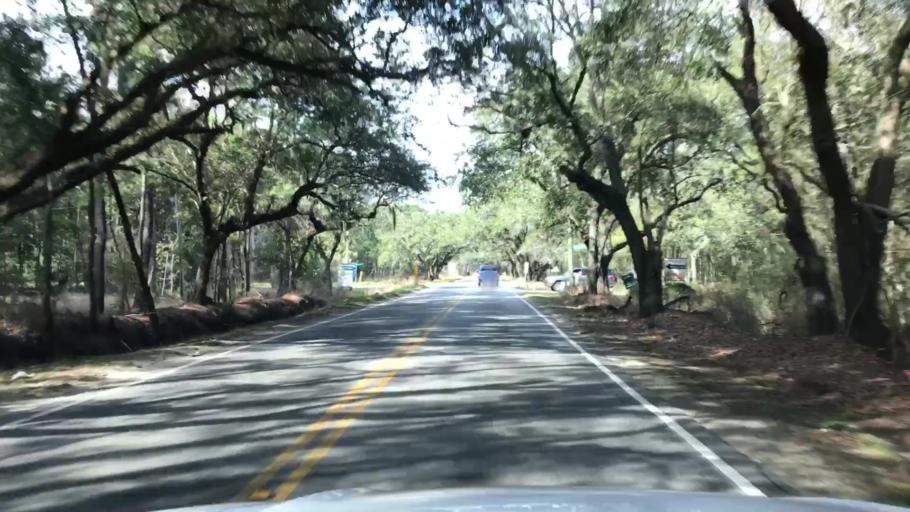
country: US
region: South Carolina
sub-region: Charleston County
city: Shell Point
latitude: 32.7541
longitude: -80.0477
